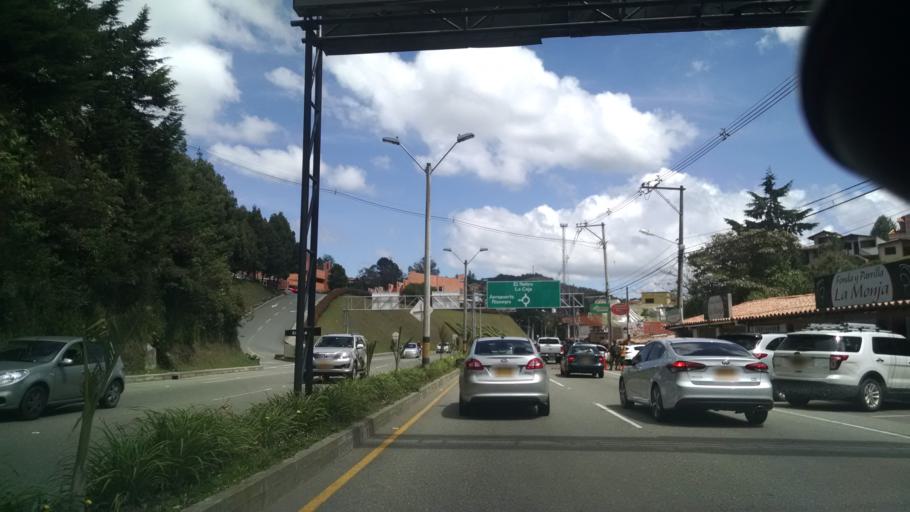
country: CO
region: Antioquia
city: Envigado
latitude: 6.1542
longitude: -75.5351
